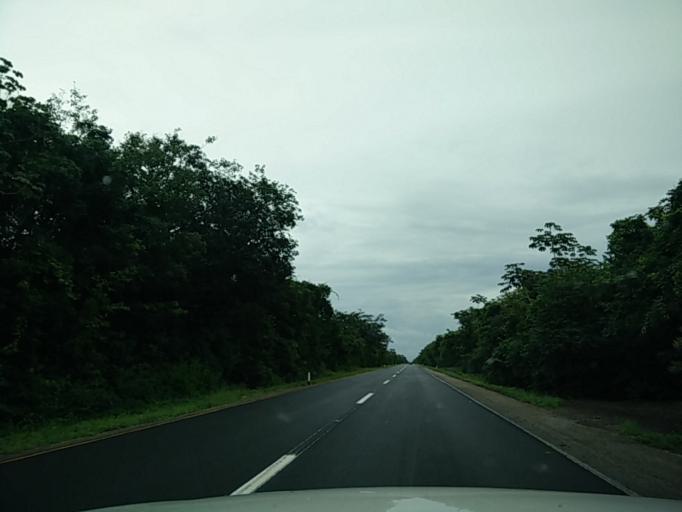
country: MX
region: Quintana Roo
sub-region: Lazaro Cardenas
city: Nuevo Xcan
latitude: 20.8823
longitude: -87.5812
